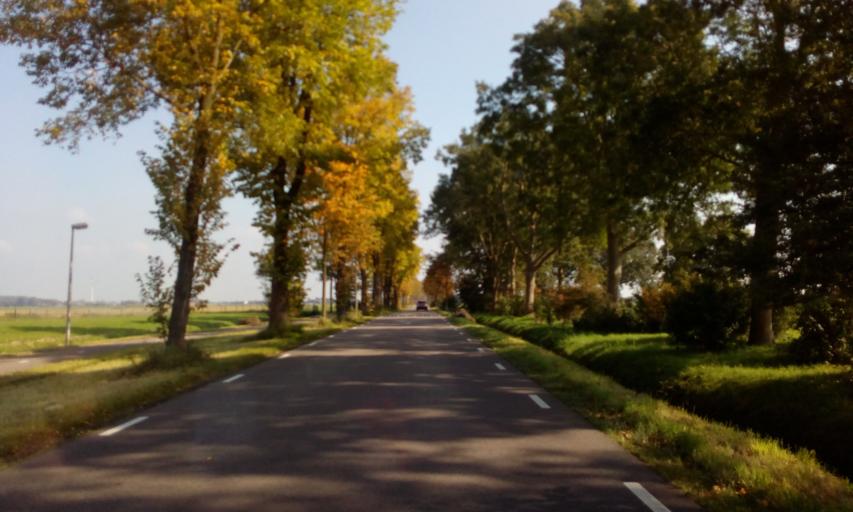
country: NL
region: South Holland
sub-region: Gemeente Leiden
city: Leiden
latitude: 52.1185
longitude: 4.5058
